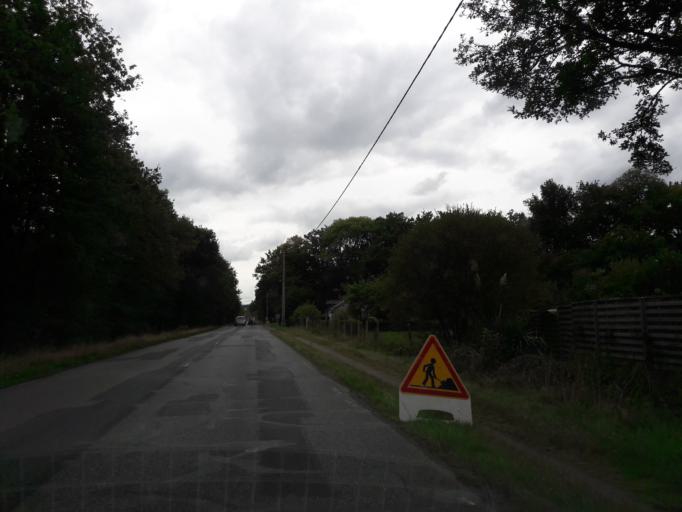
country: FR
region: Brittany
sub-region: Departement d'Ille-et-Vilaine
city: Orgeres
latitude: 48.0012
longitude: -1.6969
